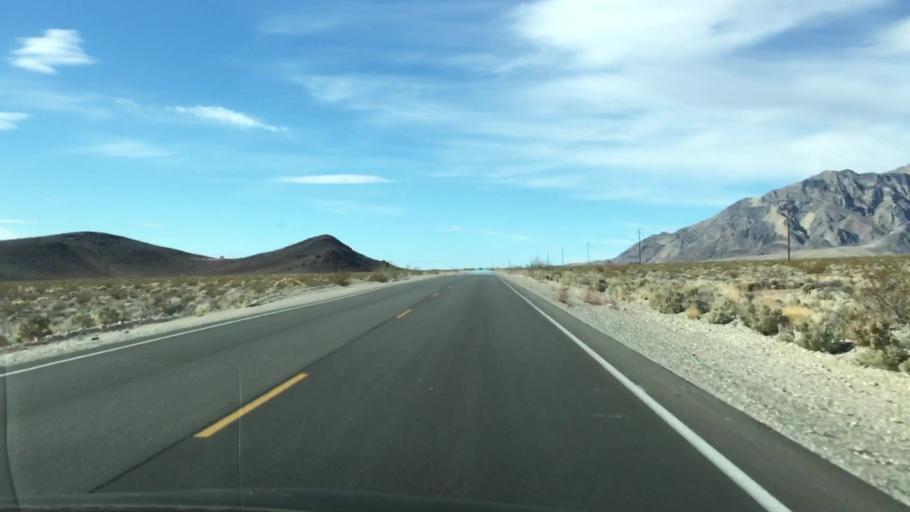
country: US
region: Nevada
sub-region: Nye County
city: Beatty
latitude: 36.3349
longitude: -116.5850
